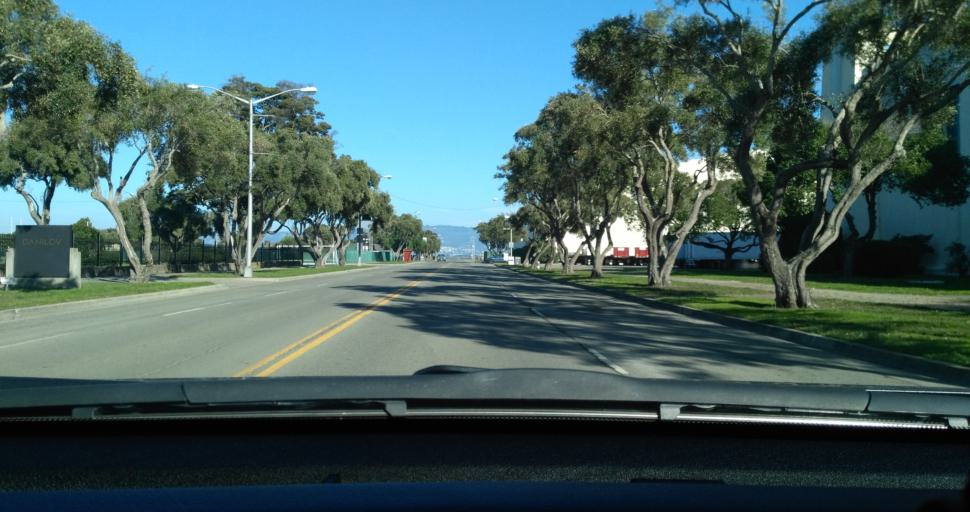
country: US
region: California
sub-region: San Francisco County
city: San Francisco
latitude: 37.8190
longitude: -122.3684
